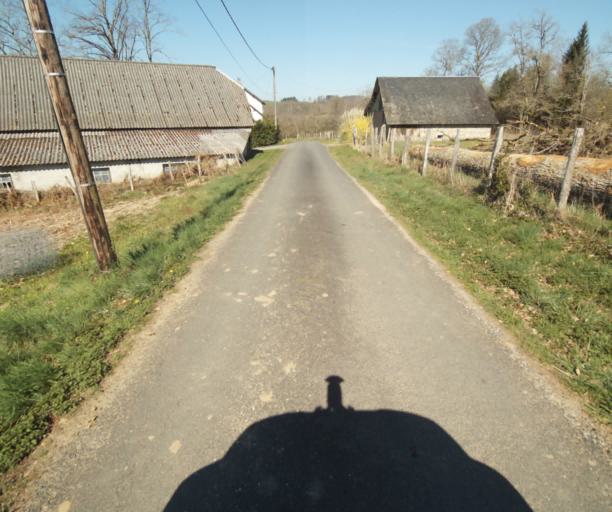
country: FR
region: Limousin
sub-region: Departement de la Correze
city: Saint-Mexant
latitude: 45.3113
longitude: 1.5997
